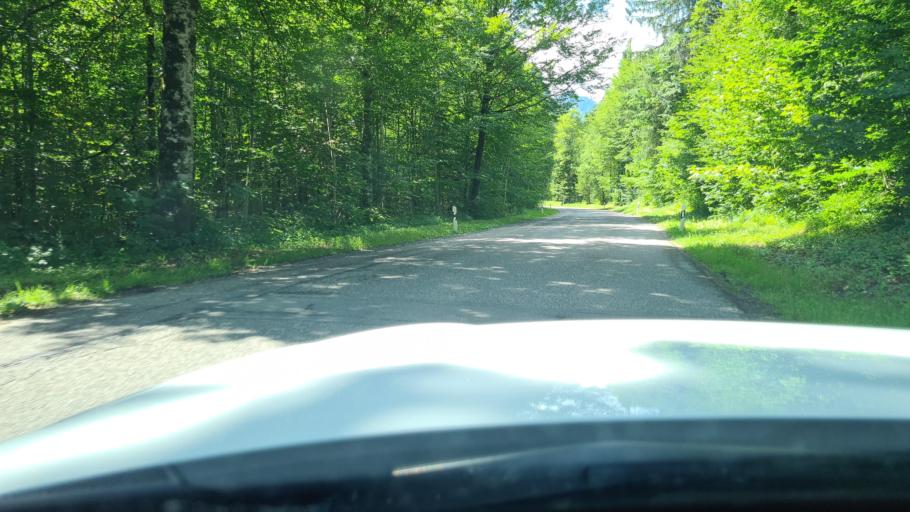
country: DE
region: Bavaria
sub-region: Swabia
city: Oberstdorf
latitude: 47.3820
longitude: 10.2815
